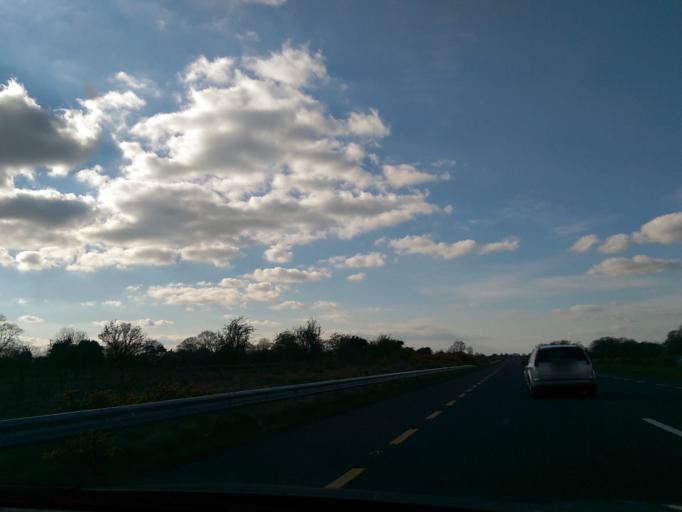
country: IE
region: Connaught
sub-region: County Galway
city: Loughrea
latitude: 53.2227
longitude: -8.5845
